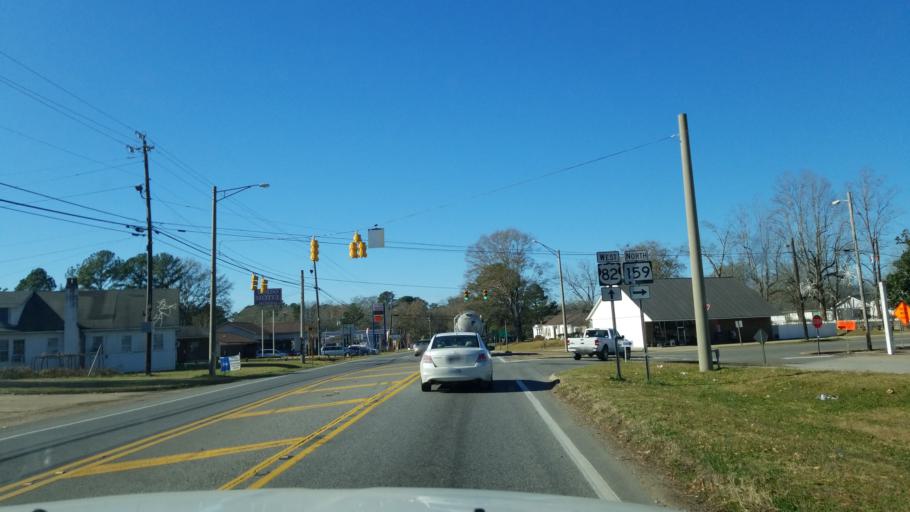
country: US
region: Alabama
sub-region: Pickens County
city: Gordo
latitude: 33.3162
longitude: -87.9026
